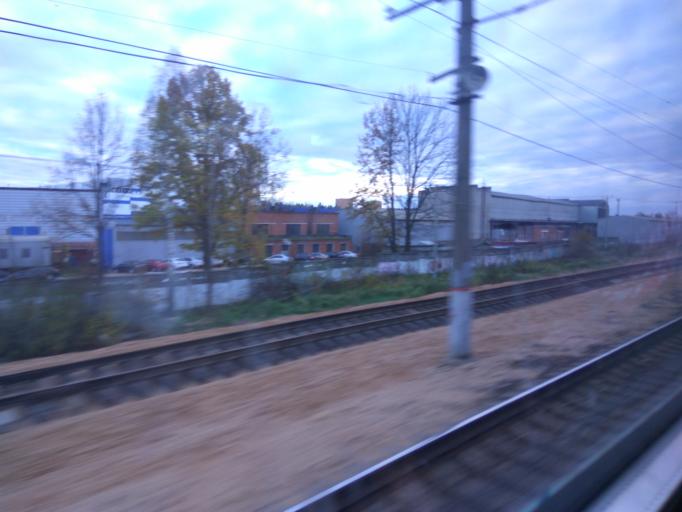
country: RU
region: Moskovskaya
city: Selyatino
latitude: 55.5204
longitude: 36.9748
